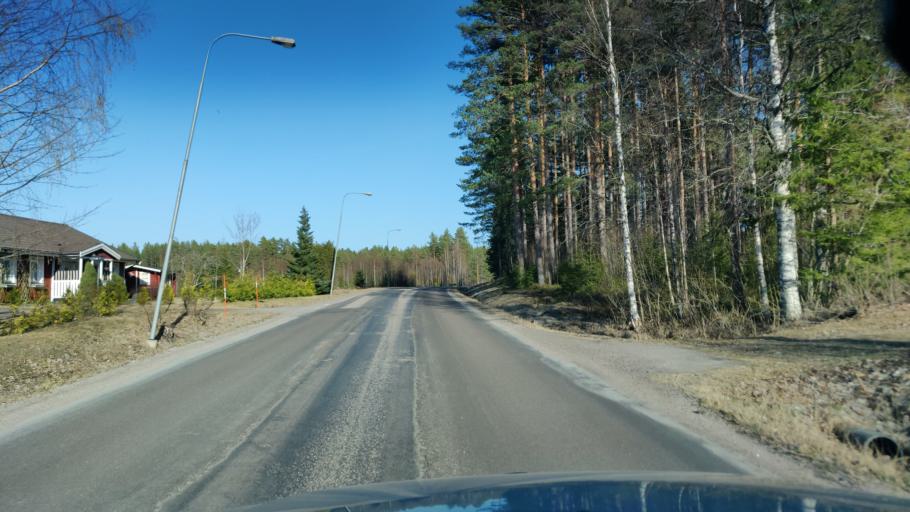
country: SE
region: Vaermland
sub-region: Sunne Kommun
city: Sunne
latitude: 59.9934
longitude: 13.2945
